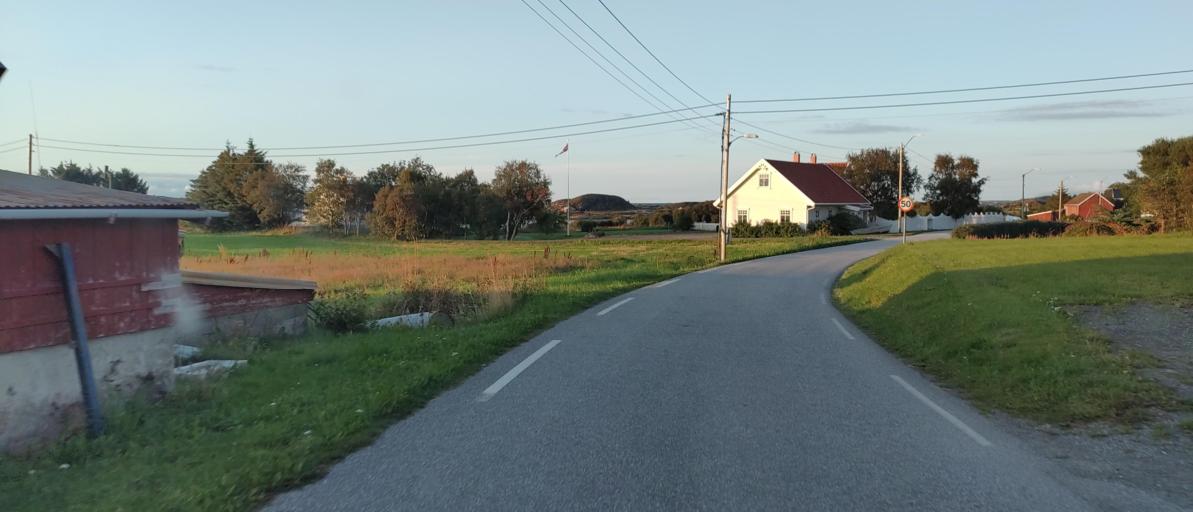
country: NO
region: More og Romsdal
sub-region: Fraena
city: Elnesvagen
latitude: 62.9975
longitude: 7.2241
